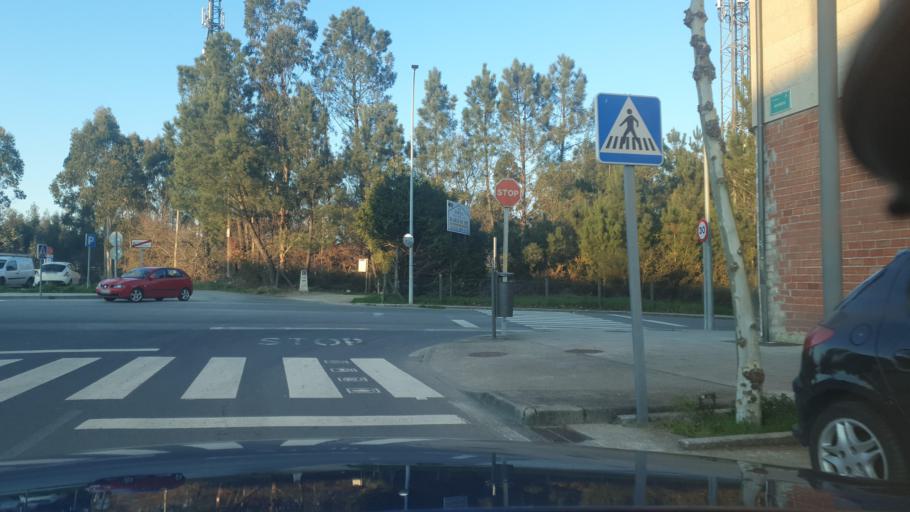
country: ES
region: Galicia
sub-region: Provincia da Coruna
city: Santiago de Compostela
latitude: 42.8482
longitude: -8.5801
